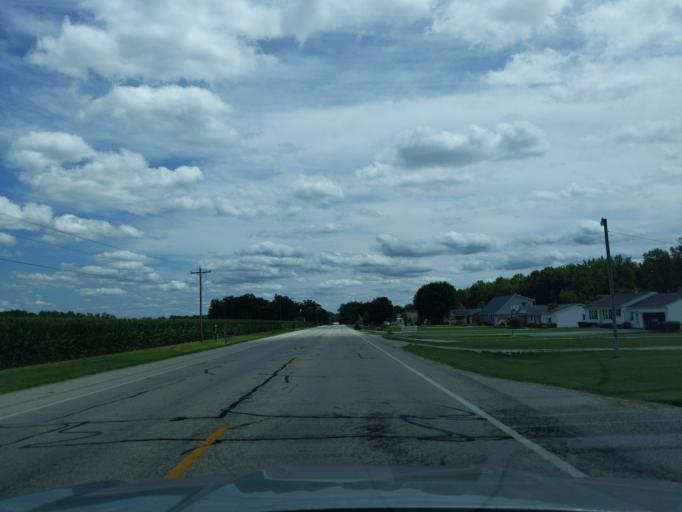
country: US
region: Indiana
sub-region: Ripley County
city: Batesville
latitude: 39.3085
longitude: -85.2639
